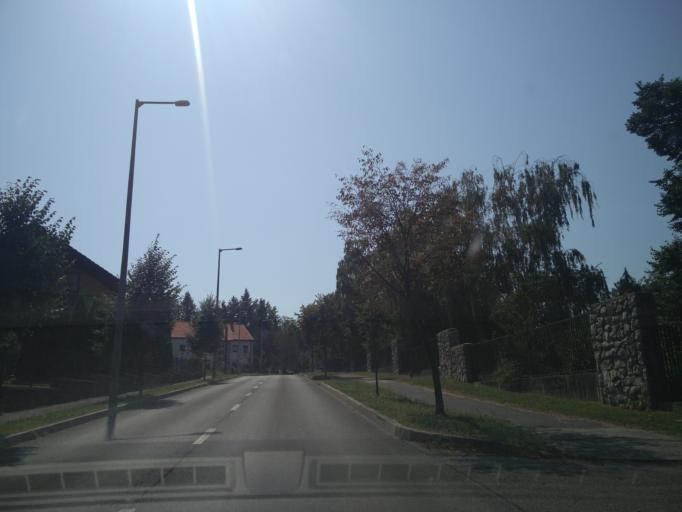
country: HU
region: Zala
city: Zalaegerszeg
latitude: 46.8310
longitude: 16.8379
